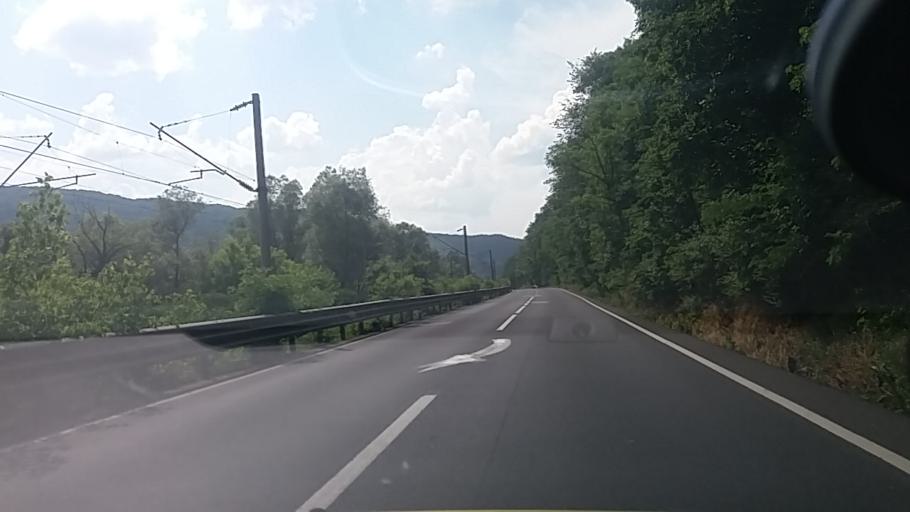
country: RO
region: Hunedoara
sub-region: Comuna Zam
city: Zam
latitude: 45.9731
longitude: 22.4464
